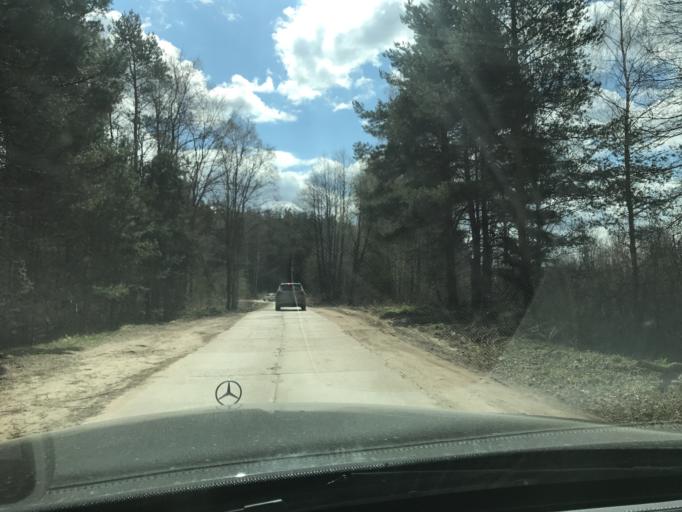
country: RU
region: Moskovskaya
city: Vereya
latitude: 55.8389
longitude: 39.0837
